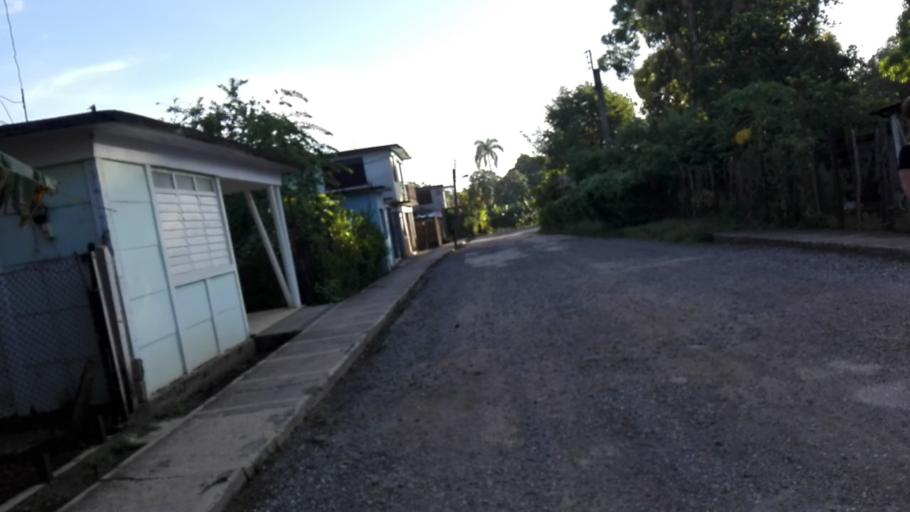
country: CU
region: Granma
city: Bartolome Maso
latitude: 20.1640
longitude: -76.9482
